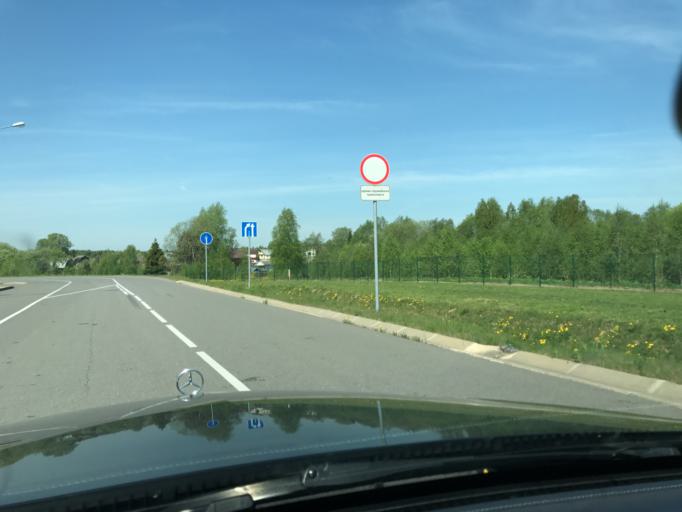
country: RU
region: Moskovskaya
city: Sychevo
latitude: 55.9990
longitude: 36.2700
